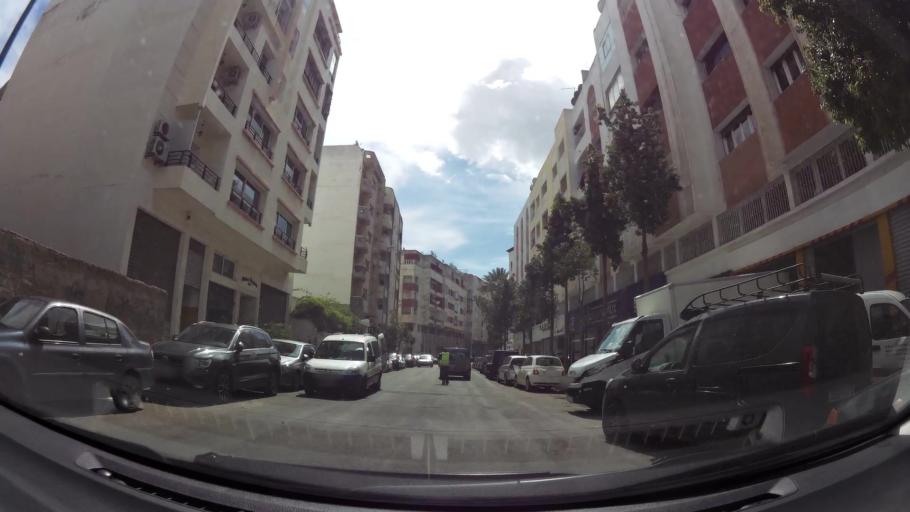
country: MA
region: Grand Casablanca
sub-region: Casablanca
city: Casablanca
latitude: 33.5789
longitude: -7.6409
